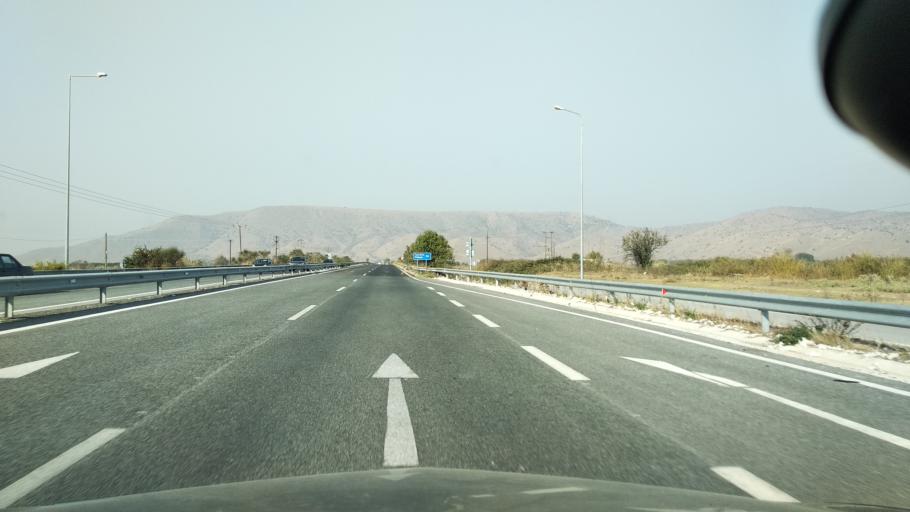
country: GR
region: Thessaly
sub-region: Trikala
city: Zarkos
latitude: 39.5950
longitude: 22.1192
